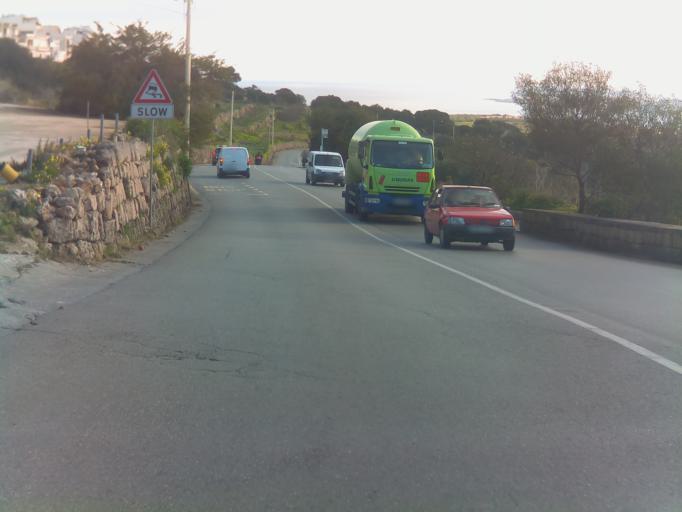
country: MT
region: Il-Mellieha
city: Mellieha
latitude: 35.9539
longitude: 14.3748
